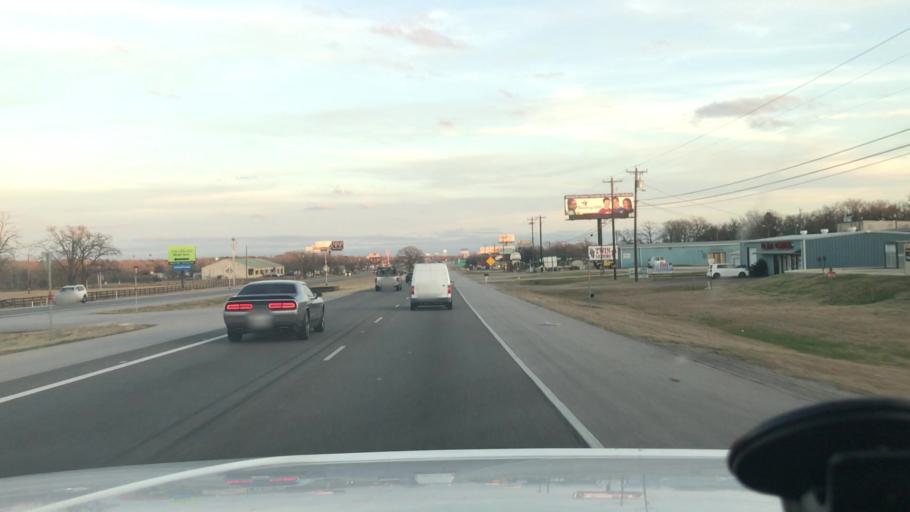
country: US
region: Texas
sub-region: Bastrop County
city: Wyldwood
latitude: 30.1201
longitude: -97.4293
